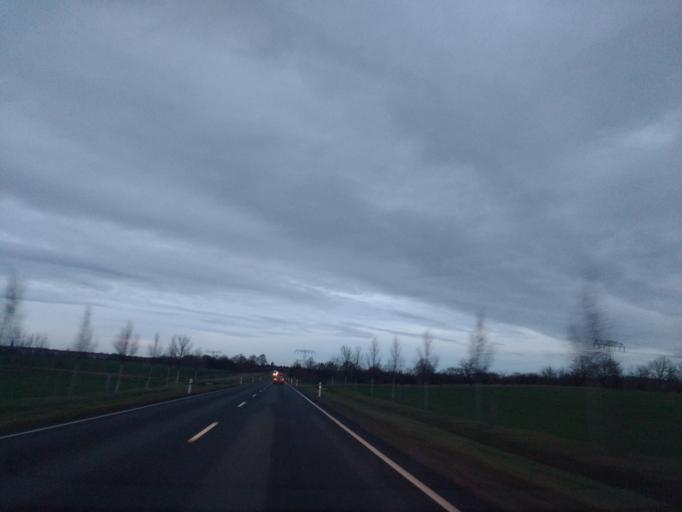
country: DE
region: Saxony-Anhalt
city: Quedlinburg
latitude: 51.7675
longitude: 11.1571
